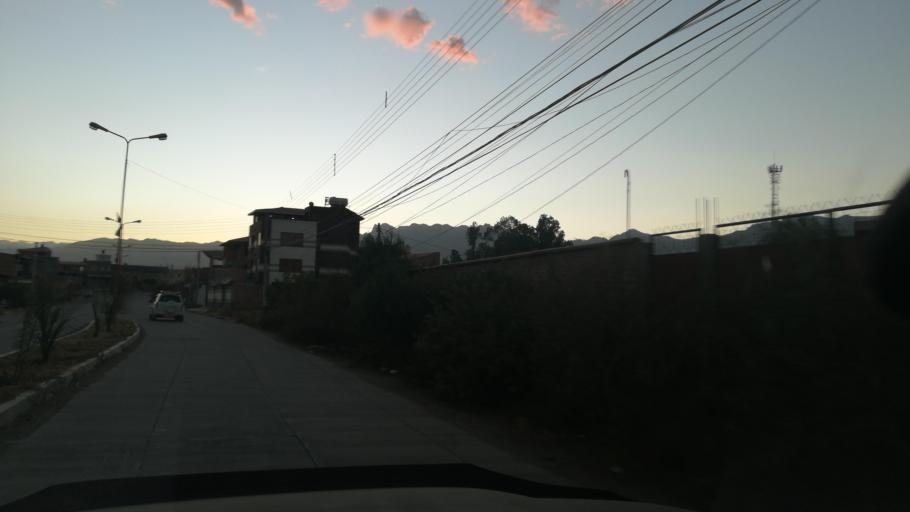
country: BO
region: Cochabamba
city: Cochabamba
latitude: -17.3835
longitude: -66.2194
